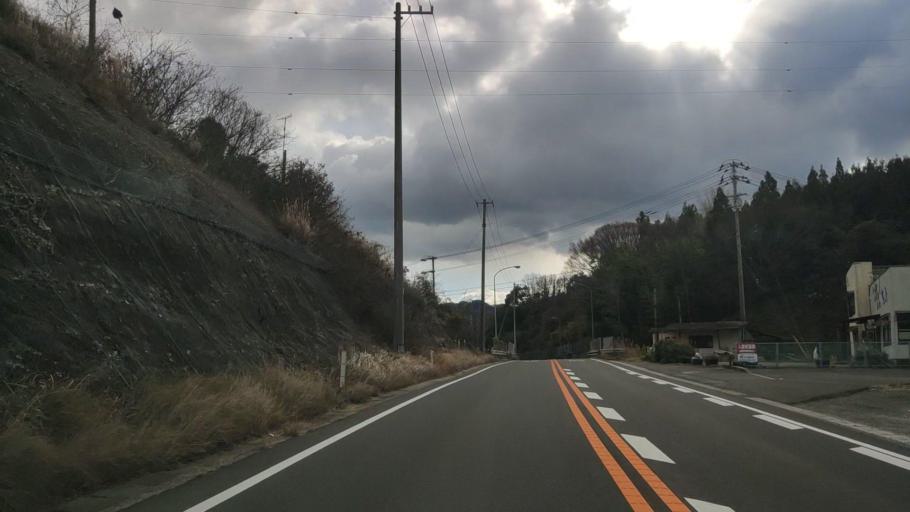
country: JP
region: Ehime
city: Hojo
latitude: 34.0619
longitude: 132.9148
